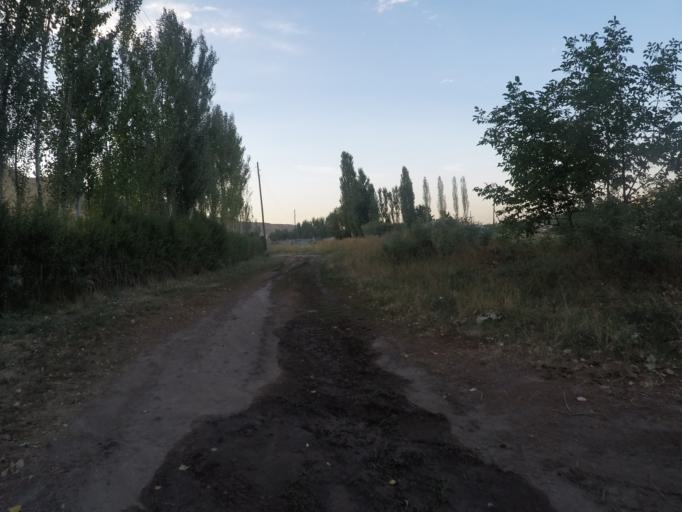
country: KG
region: Chuy
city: Bishkek
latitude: 42.7646
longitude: 74.6386
